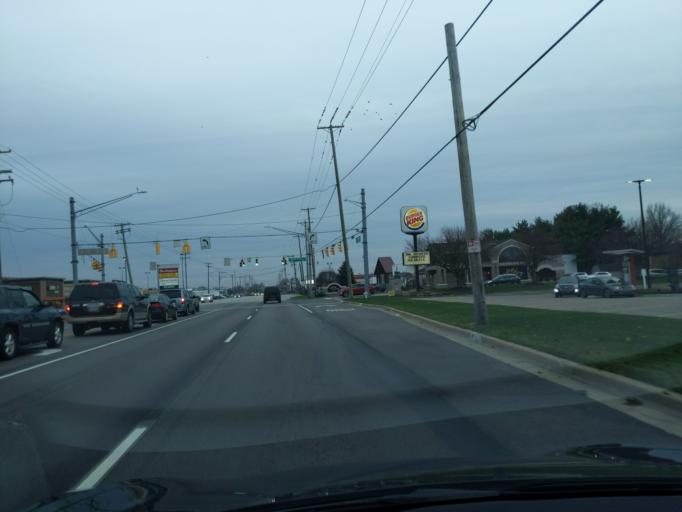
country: US
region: Indiana
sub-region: Saint Joseph County
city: Georgetown
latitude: 41.7134
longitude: -86.1877
